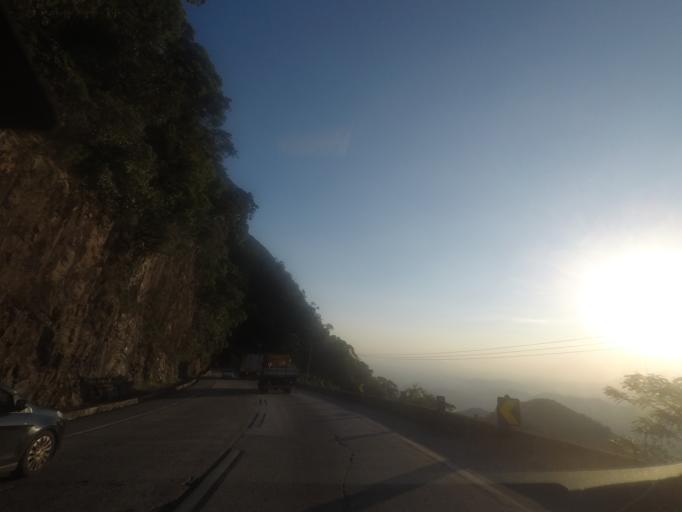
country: BR
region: Rio de Janeiro
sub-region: Petropolis
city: Petropolis
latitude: -22.5219
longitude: -43.2376
